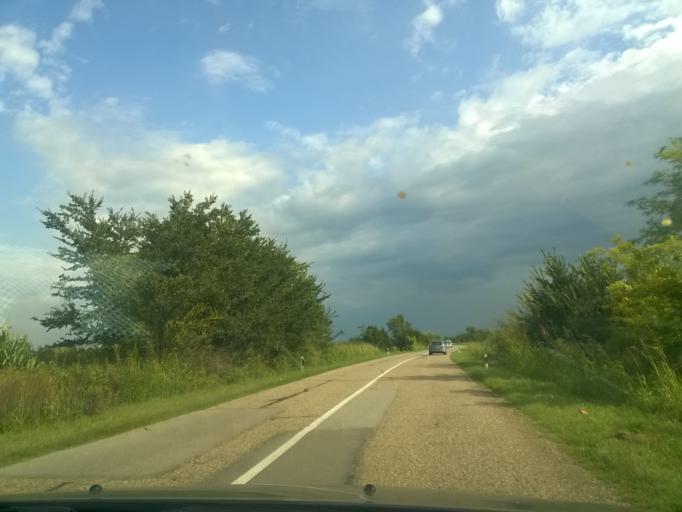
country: RS
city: Uzdin
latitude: 45.1717
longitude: 20.6176
